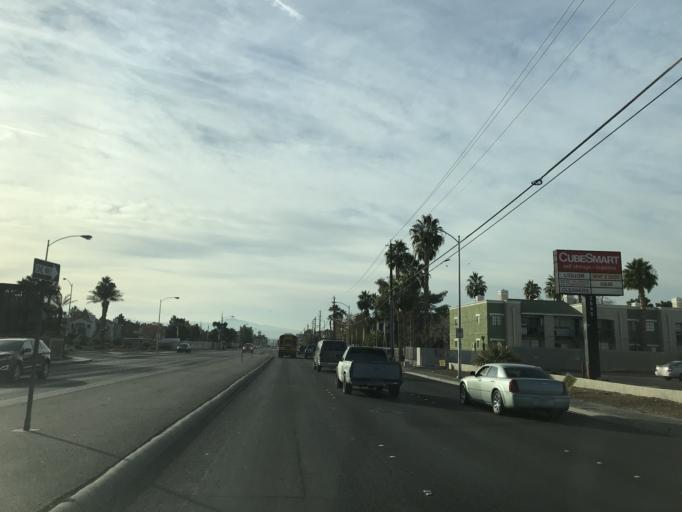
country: US
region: Nevada
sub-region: Clark County
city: Winchester
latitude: 36.1420
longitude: -115.0655
